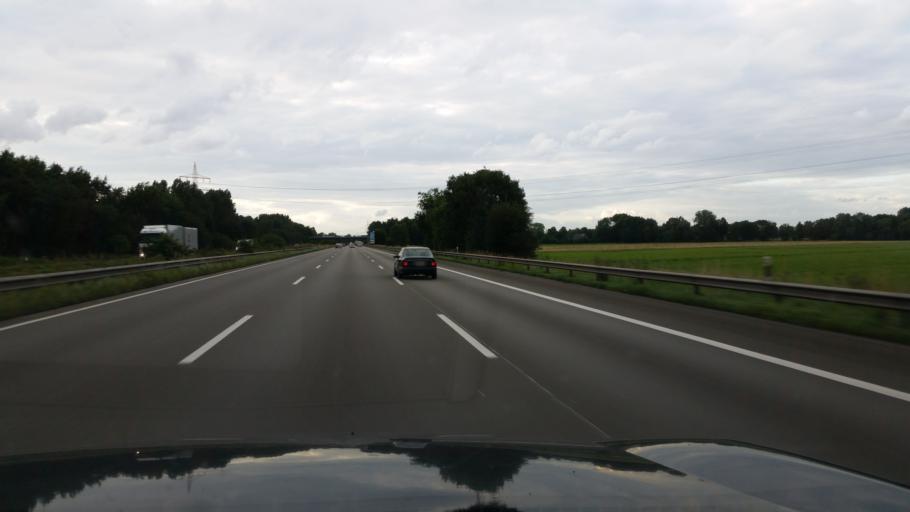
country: DE
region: Hamburg
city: Harburg
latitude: 53.4339
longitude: 10.0330
